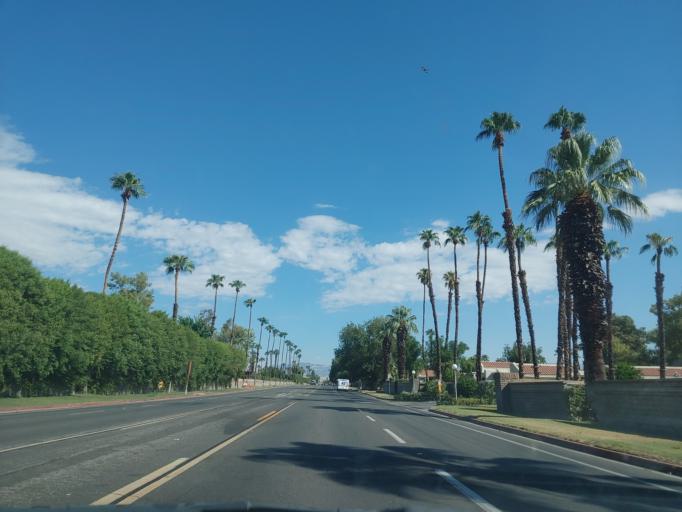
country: US
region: California
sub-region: Riverside County
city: Cathedral City
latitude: 33.7958
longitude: -116.4667
